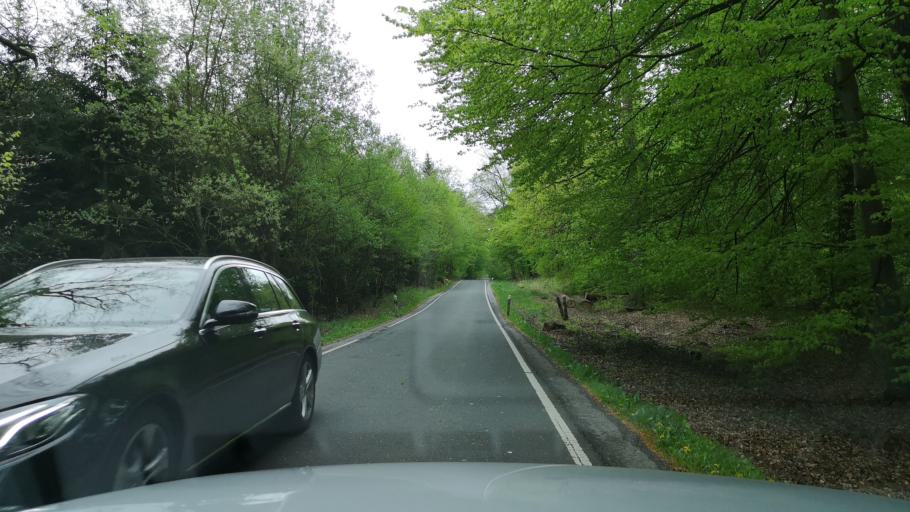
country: DE
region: North Rhine-Westphalia
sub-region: Regierungsbezirk Arnsberg
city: Frondenberg
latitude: 51.4560
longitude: 7.7076
